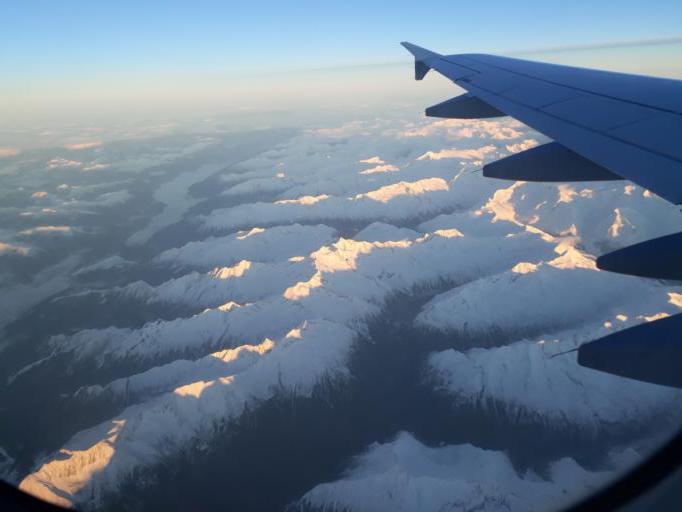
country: AT
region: Tyrol
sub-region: Politischer Bezirk Schwaz
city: Mayrhofen
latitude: 47.1176
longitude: 11.8774
